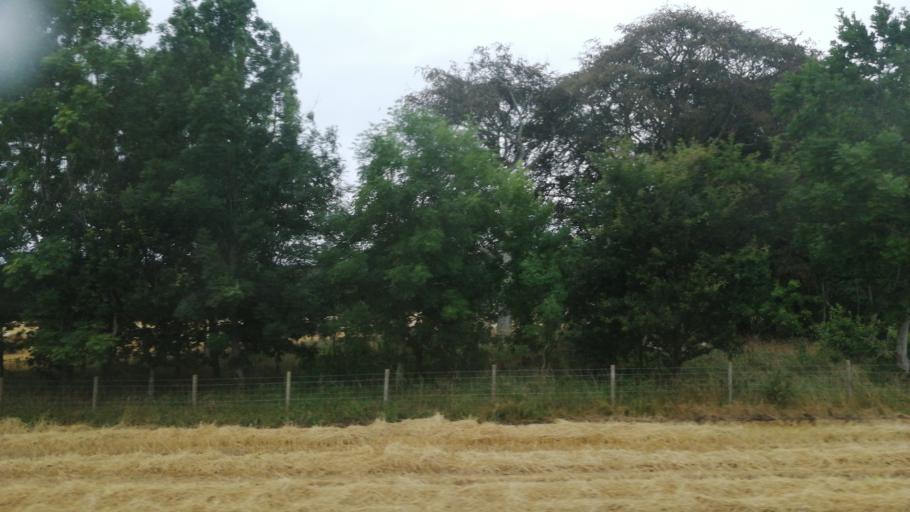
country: GB
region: Scotland
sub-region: Highland
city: Alness
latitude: 57.8572
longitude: -4.3045
